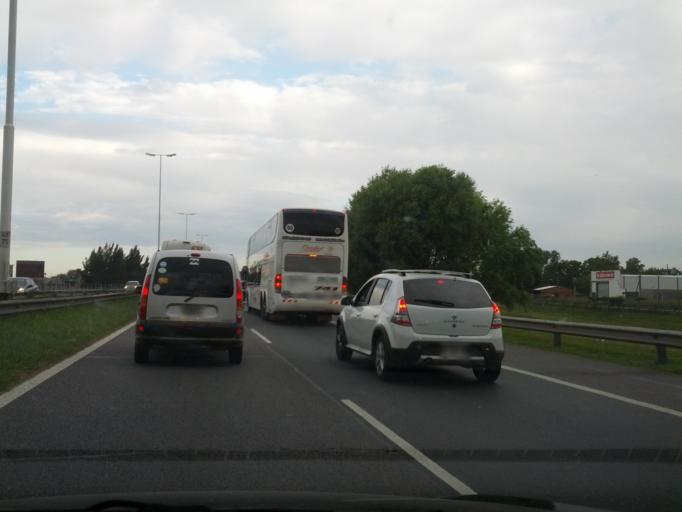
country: AR
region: Buenos Aires
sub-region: Partido de General Rodriguez
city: General Rodriguez
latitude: -34.6039
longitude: -58.8945
